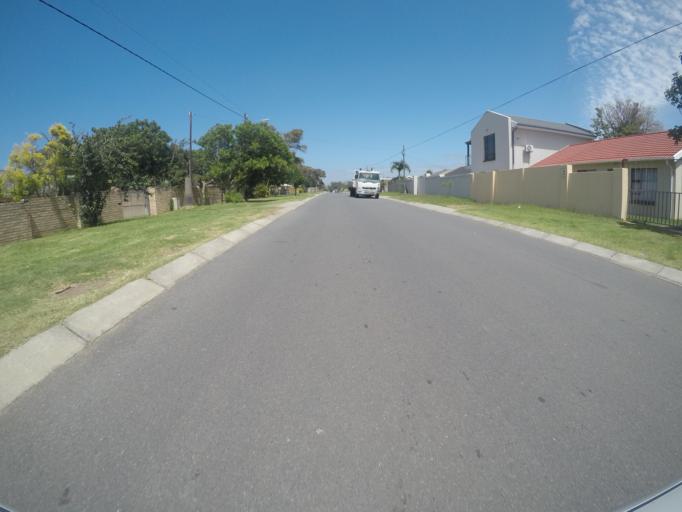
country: ZA
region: Eastern Cape
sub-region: Buffalo City Metropolitan Municipality
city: East London
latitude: -32.9500
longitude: 27.9990
